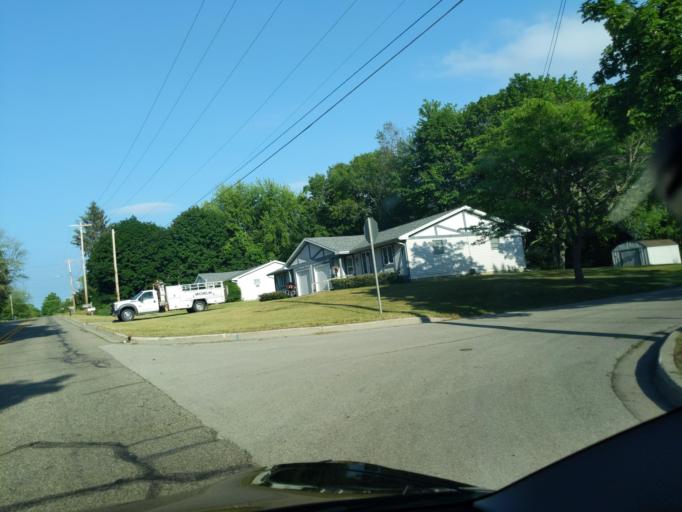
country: US
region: Michigan
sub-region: Muskegon County
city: Whitehall
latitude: 43.4034
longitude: -86.3338
